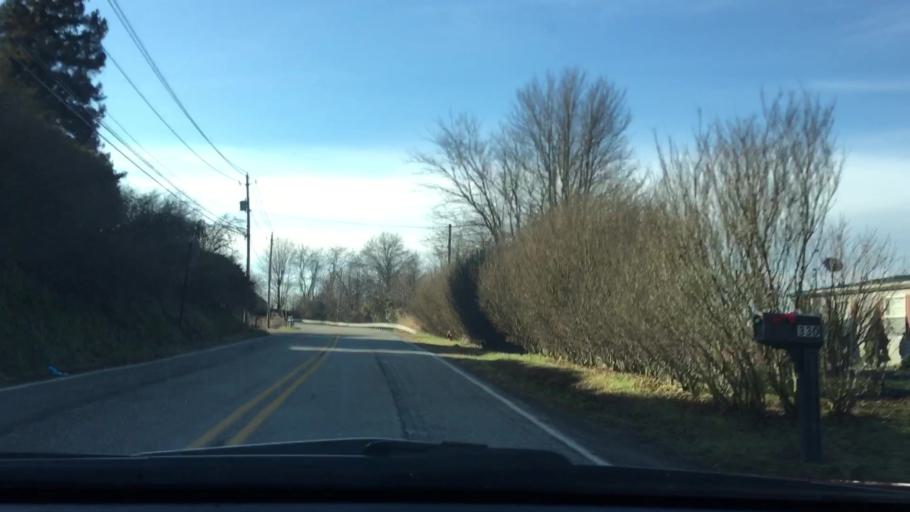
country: US
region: Pennsylvania
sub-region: Westmoreland County
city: Irwin
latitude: 40.2885
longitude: -79.6913
